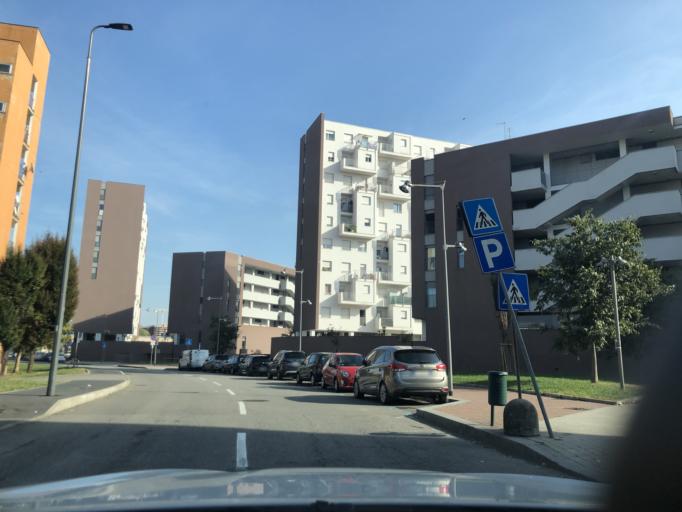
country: IT
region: Lombardy
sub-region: Citta metropolitana di Milano
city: Pero
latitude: 45.5033
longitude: 9.1060
